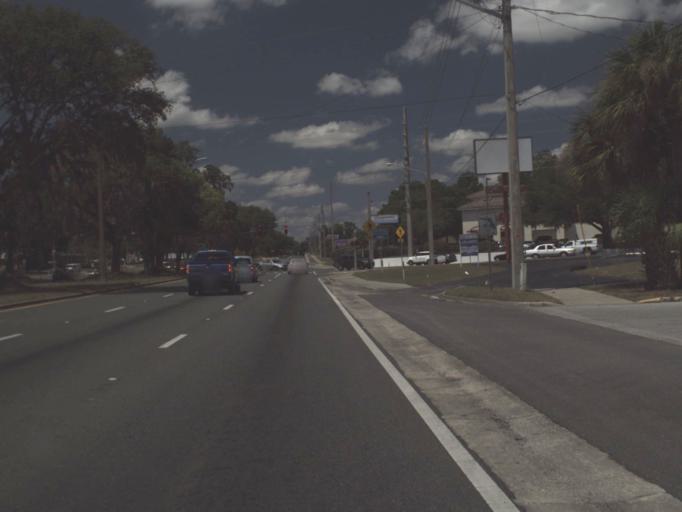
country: US
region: Florida
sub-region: Marion County
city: Ocala
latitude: 29.1984
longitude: -82.0858
